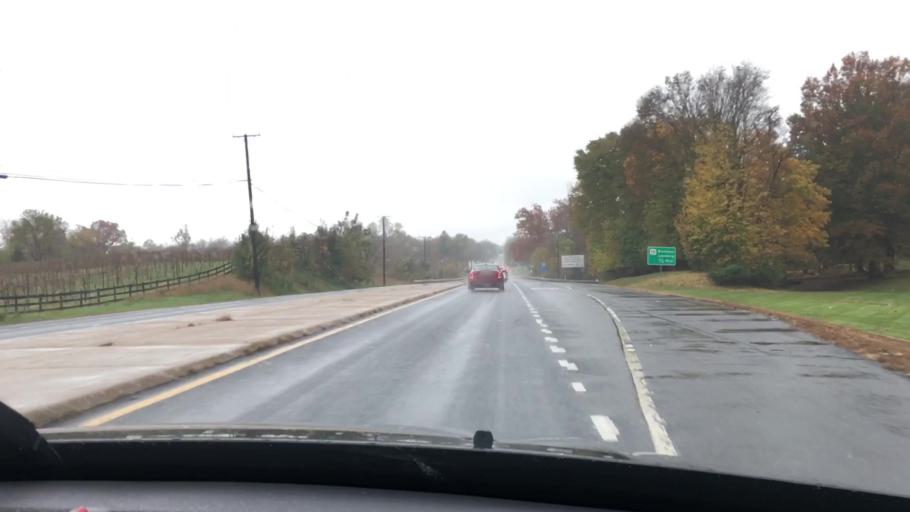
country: US
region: Virginia
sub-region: Loudoun County
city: Leesburg
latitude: 39.1446
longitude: -77.5442
